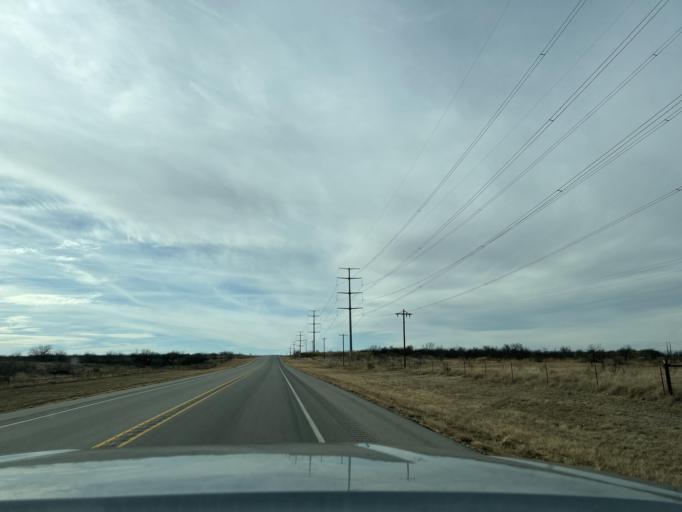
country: US
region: Texas
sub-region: Jones County
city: Stamford
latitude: 32.7503
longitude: -99.6373
